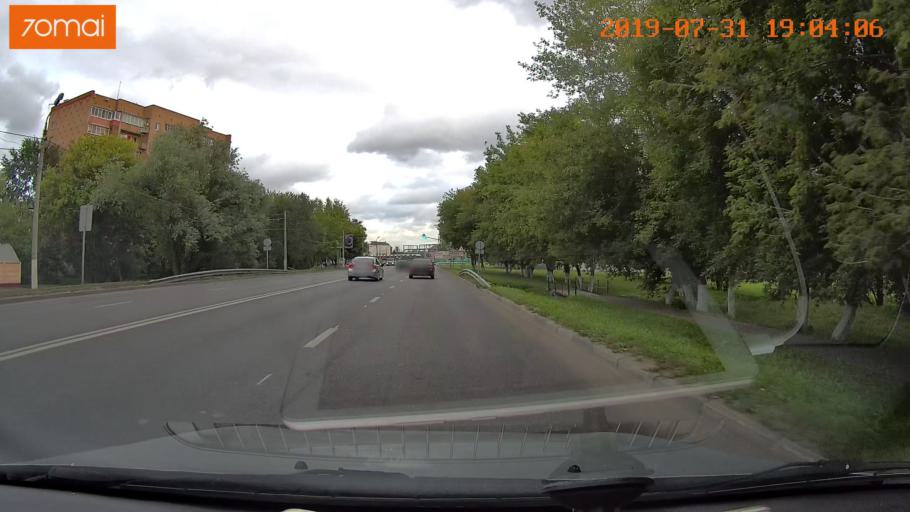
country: RU
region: Moskovskaya
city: Raduzhnyy
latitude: 55.1109
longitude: 38.7393
